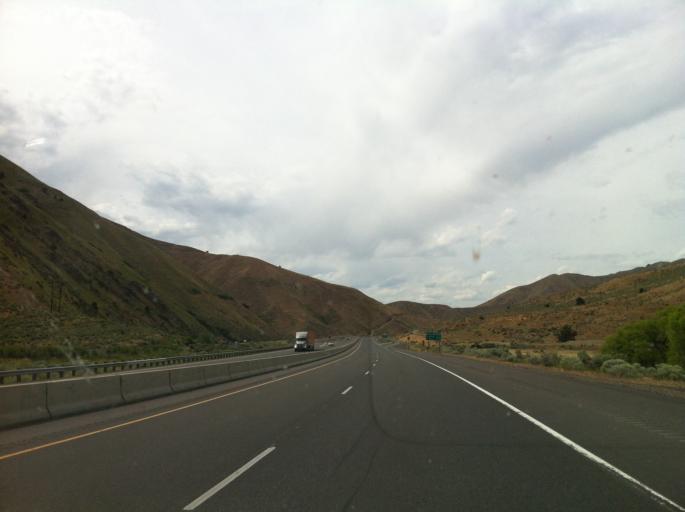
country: US
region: Idaho
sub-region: Washington County
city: Weiser
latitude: 44.4237
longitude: -117.3121
